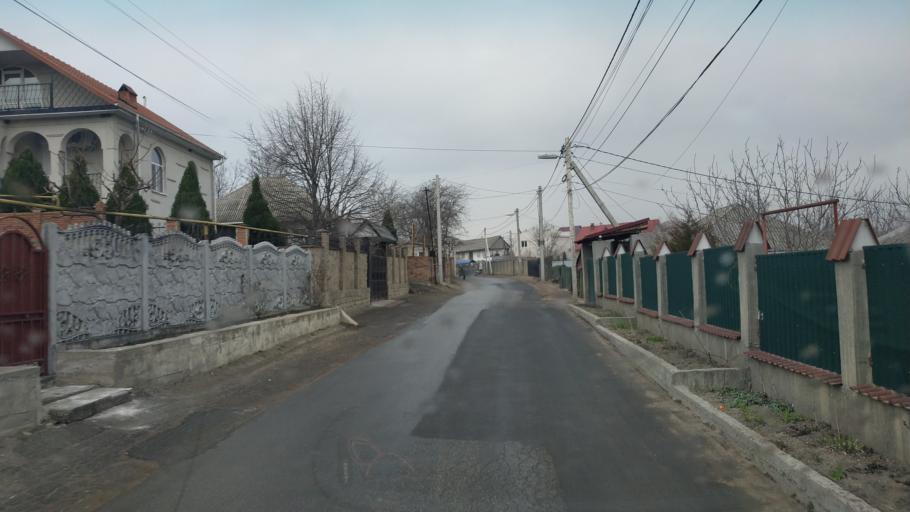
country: MD
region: Chisinau
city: Singera
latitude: 46.9092
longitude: 28.9623
